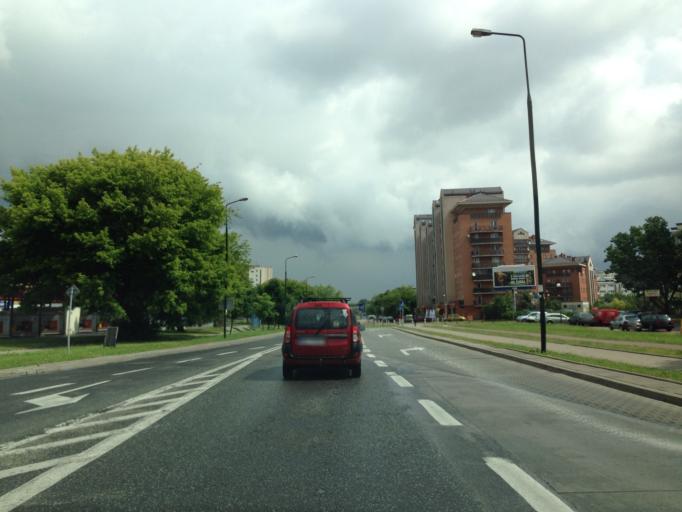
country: PL
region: Masovian Voivodeship
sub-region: Warszawa
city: Bielany
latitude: 52.2660
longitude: 20.9455
